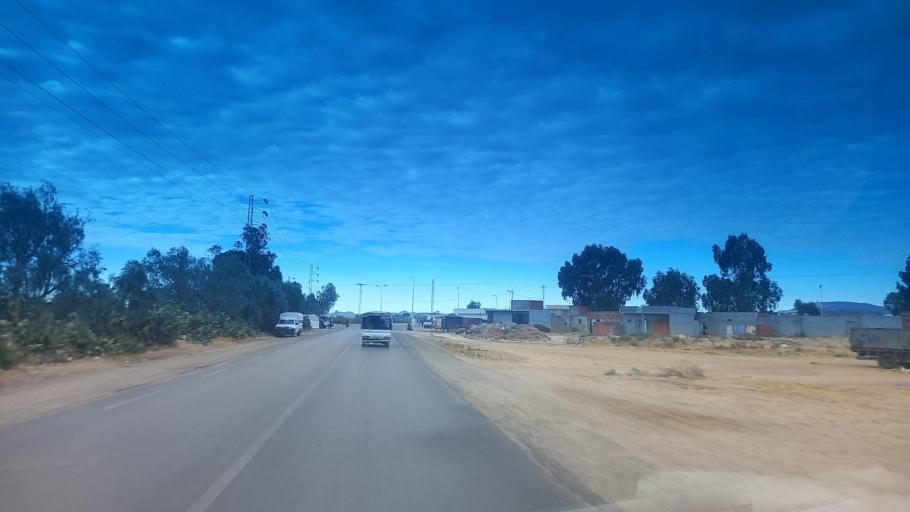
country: TN
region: Al Qasrayn
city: Kasserine
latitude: 35.2603
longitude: 9.0926
